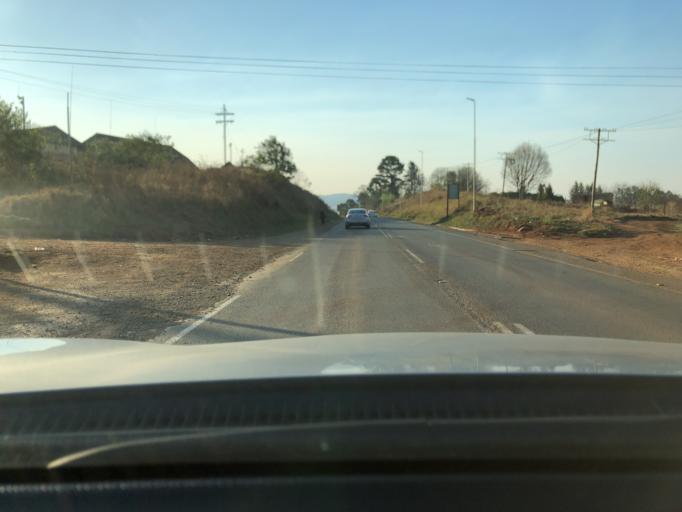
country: ZA
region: KwaZulu-Natal
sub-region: Sisonke District Municipality
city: Ixopo
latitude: -30.1508
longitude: 30.0743
